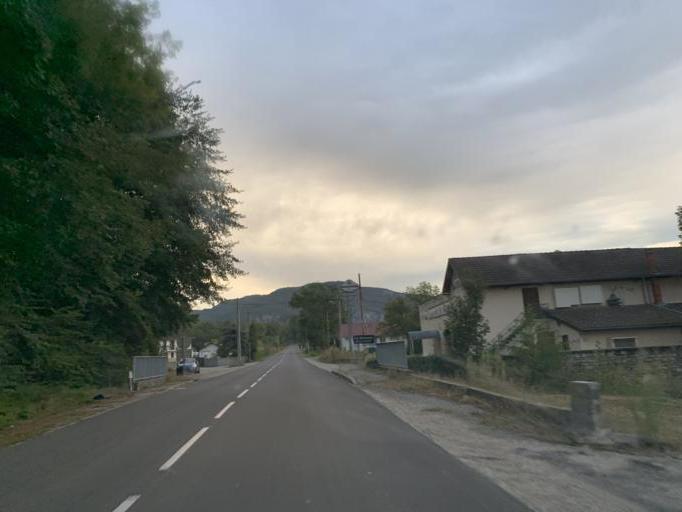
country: FR
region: Rhone-Alpes
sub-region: Departement de l'Isere
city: Creys-Mepieu
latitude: 45.7099
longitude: 5.5578
